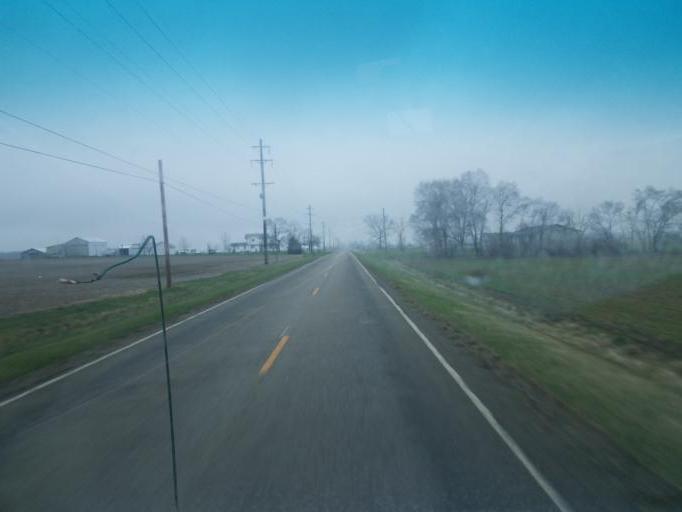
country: US
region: Ohio
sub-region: Defiance County
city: Hicksville
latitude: 41.3518
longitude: -84.7670
